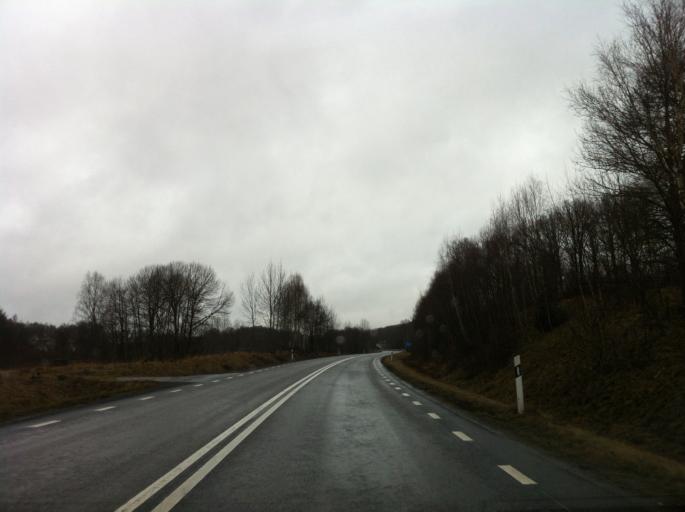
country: SE
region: Blekinge
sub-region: Olofstroms Kommun
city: Olofstroem
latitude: 56.3434
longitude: 14.4904
